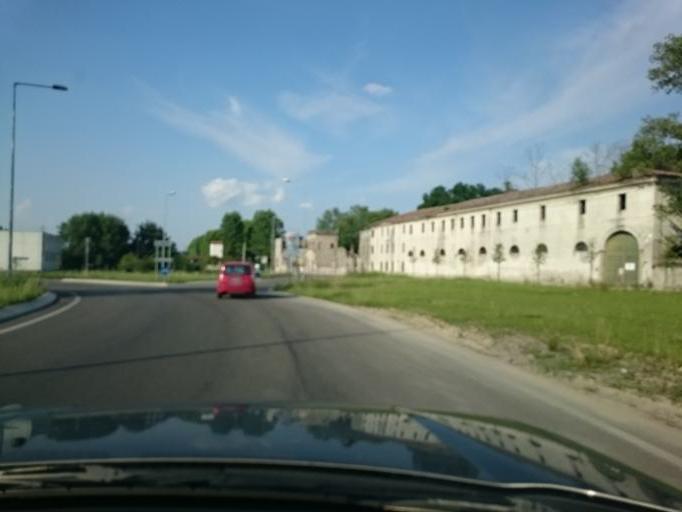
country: IT
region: Veneto
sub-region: Provincia di Padova
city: Abano Terme
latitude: 45.3591
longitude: 11.8111
